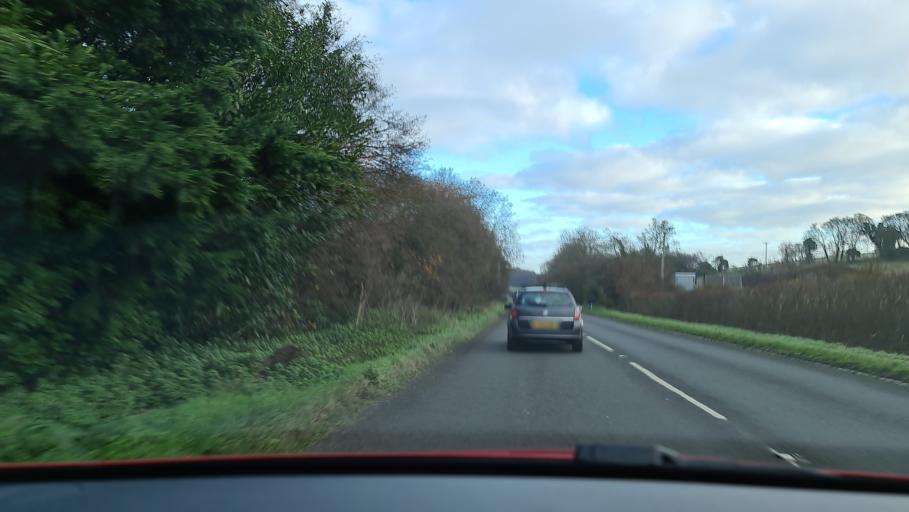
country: GB
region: England
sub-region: Buckinghamshire
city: Amersham
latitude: 51.6546
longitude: -0.6387
